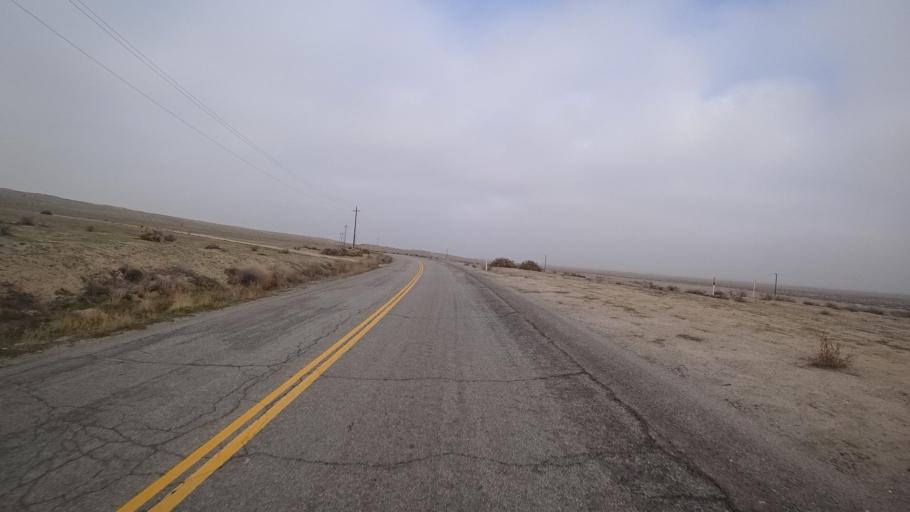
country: US
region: California
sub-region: Kern County
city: Maricopa
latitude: 35.1384
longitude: -119.3430
